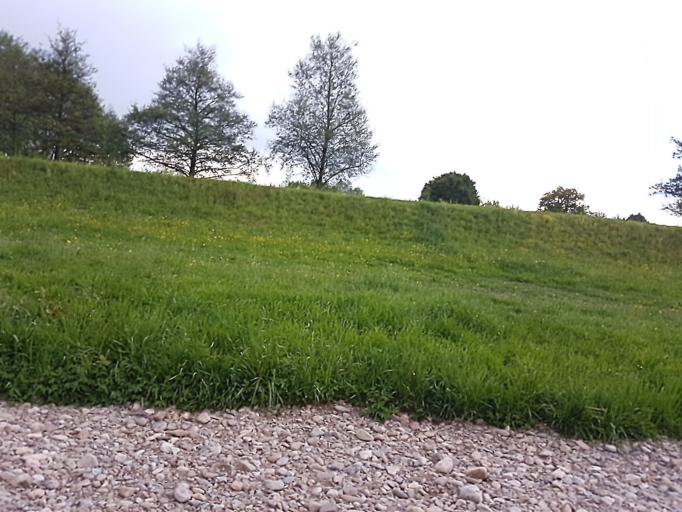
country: DE
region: Baden-Wuerttemberg
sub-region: Freiburg Region
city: Teningen
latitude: 48.1380
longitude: 7.7939
